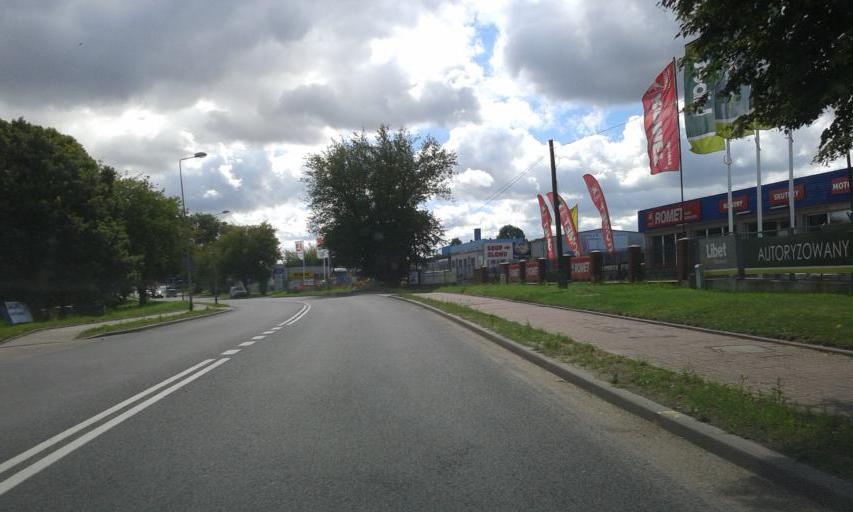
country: PL
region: West Pomeranian Voivodeship
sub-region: Powiat walecki
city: Walcz
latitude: 53.2647
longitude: 16.4896
